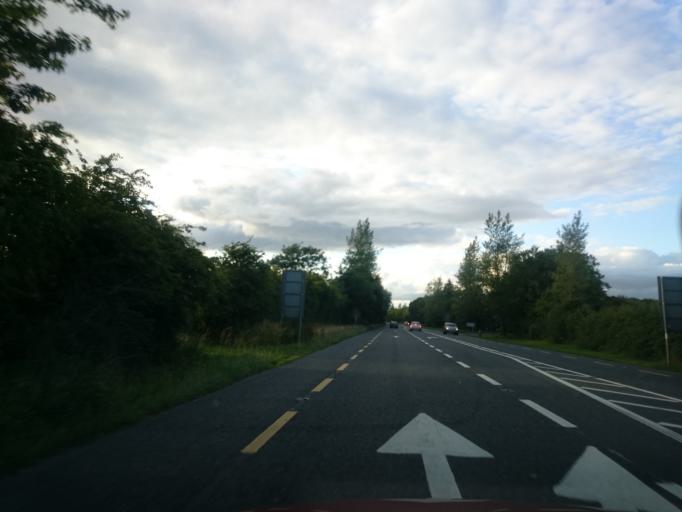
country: IE
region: Leinster
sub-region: Loch Garman
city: Enniscorthy
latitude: 52.4297
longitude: -6.5332
